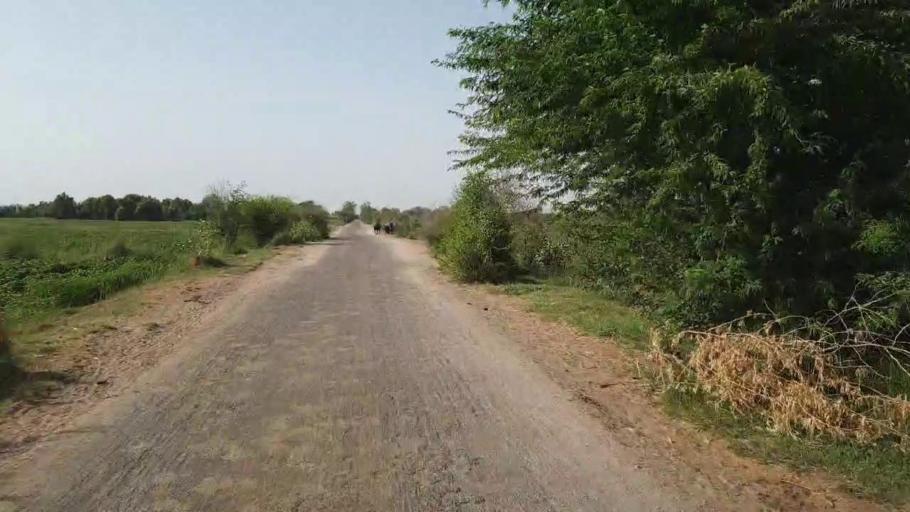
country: PK
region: Sindh
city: Kandiari
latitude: 26.6876
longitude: 68.9645
